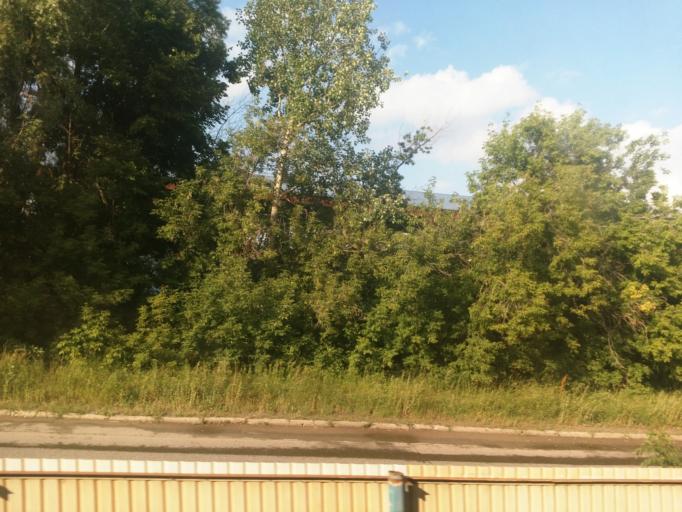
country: RU
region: Tatarstan
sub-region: Gorod Kazan'
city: Kazan
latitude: 55.8053
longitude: 49.0576
